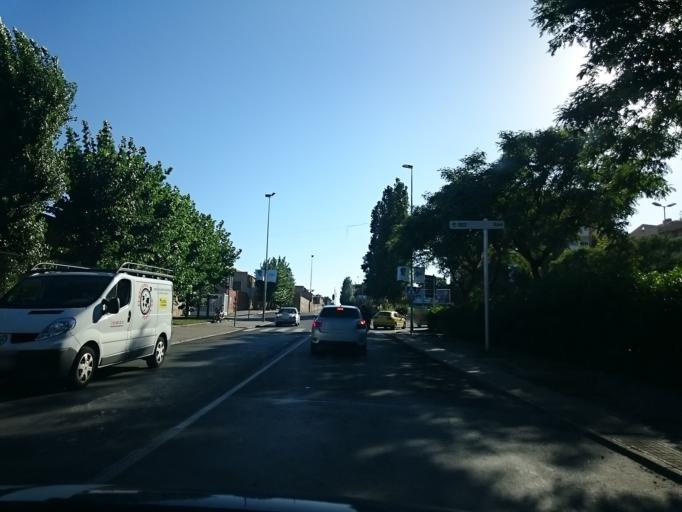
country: ES
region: Catalonia
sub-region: Provincia de Barcelona
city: Viladecans
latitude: 41.3086
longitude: 2.0135
